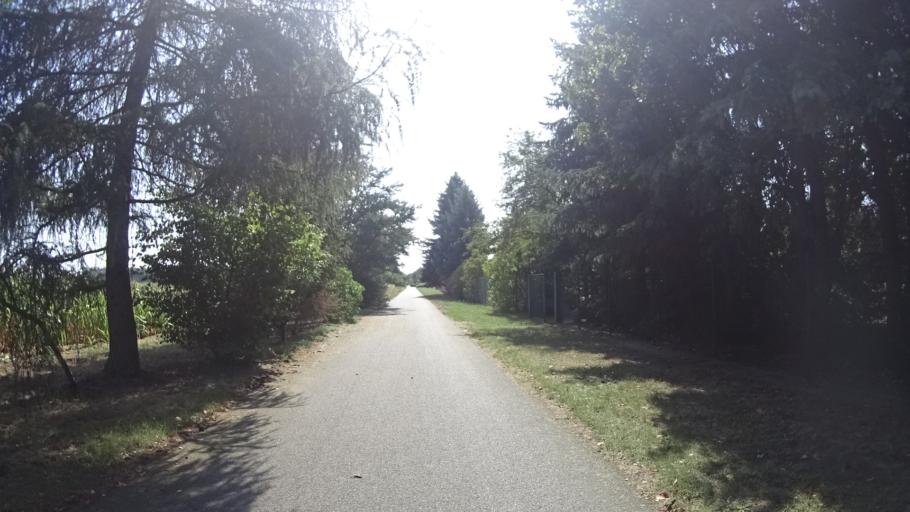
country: DE
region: Brandenburg
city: Werben
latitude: 51.8112
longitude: 14.1989
